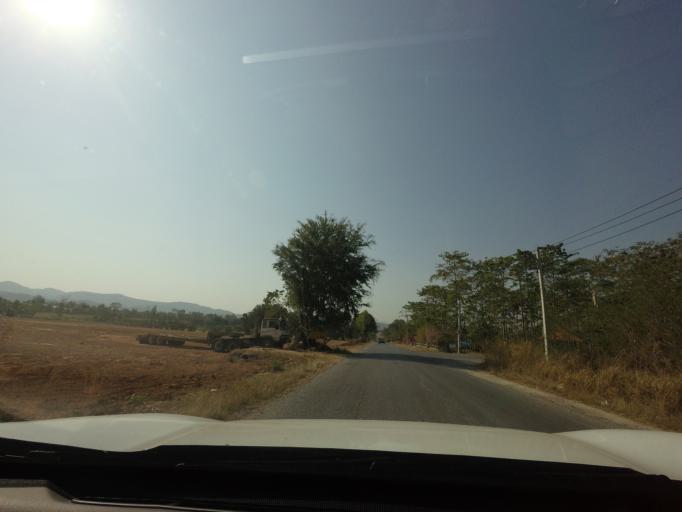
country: TH
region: Nakhon Ratchasima
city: Pak Chong
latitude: 14.6214
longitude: 101.4846
